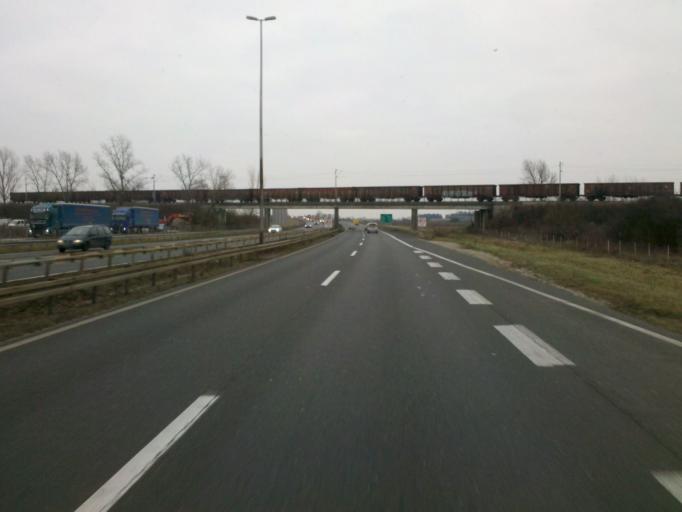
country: HR
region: Grad Zagreb
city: Zadvorsko
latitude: 45.7525
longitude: 15.9080
